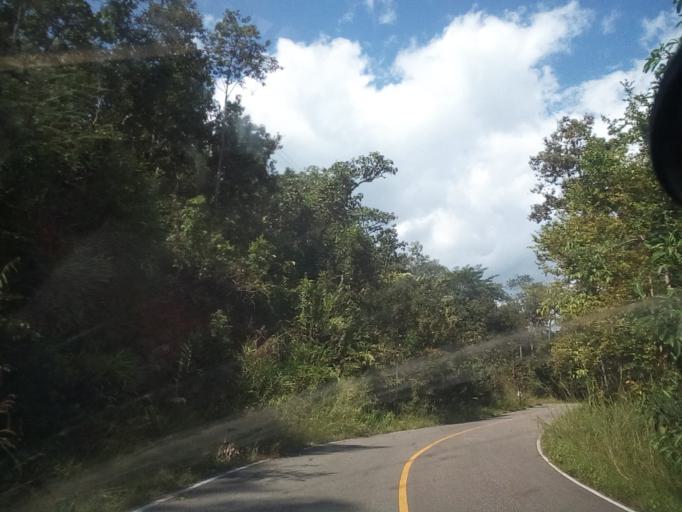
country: TH
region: Chiang Mai
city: Samoeng
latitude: 18.8732
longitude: 98.6896
